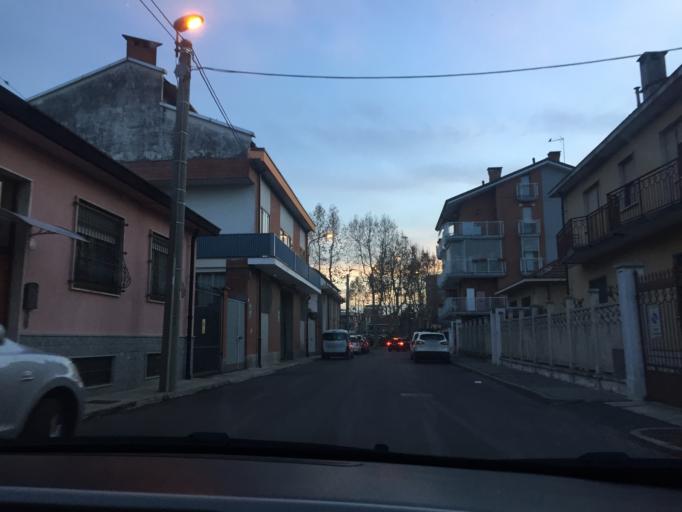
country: IT
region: Piedmont
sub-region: Provincia di Torino
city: Collegno
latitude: 45.0776
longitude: 7.6031
